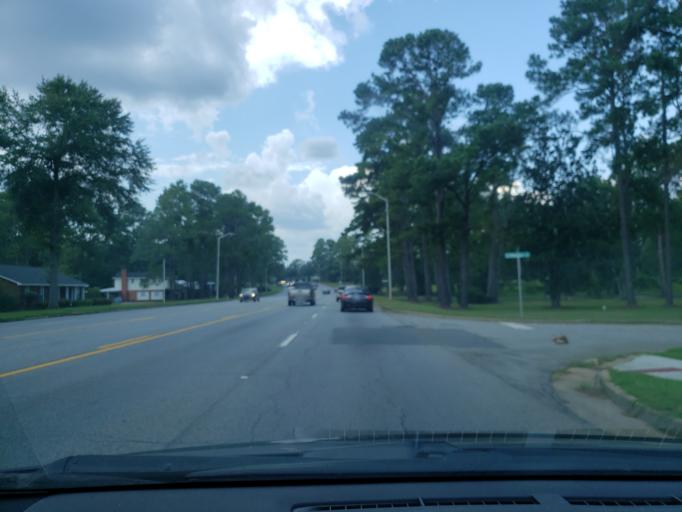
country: US
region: Georgia
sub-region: Dougherty County
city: Albany
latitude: 31.5937
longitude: -84.1935
